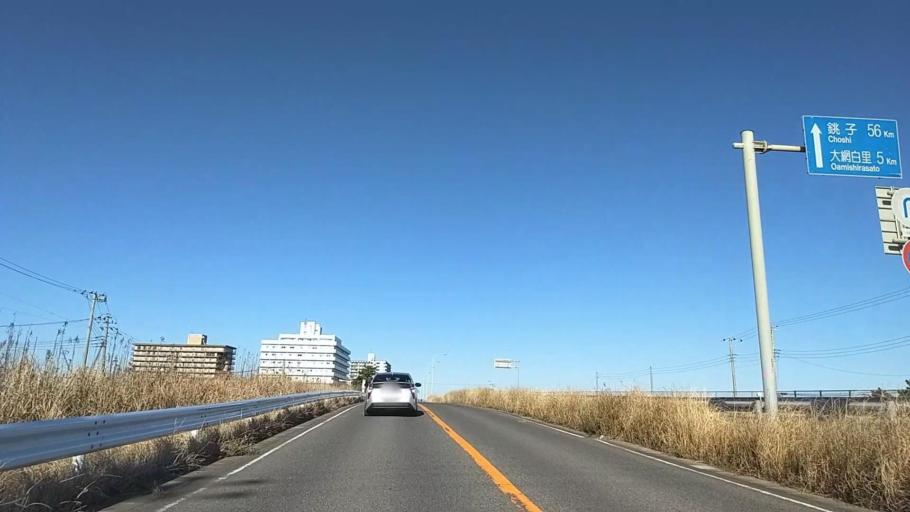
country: JP
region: Chiba
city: Mobara
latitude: 35.4479
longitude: 140.4017
